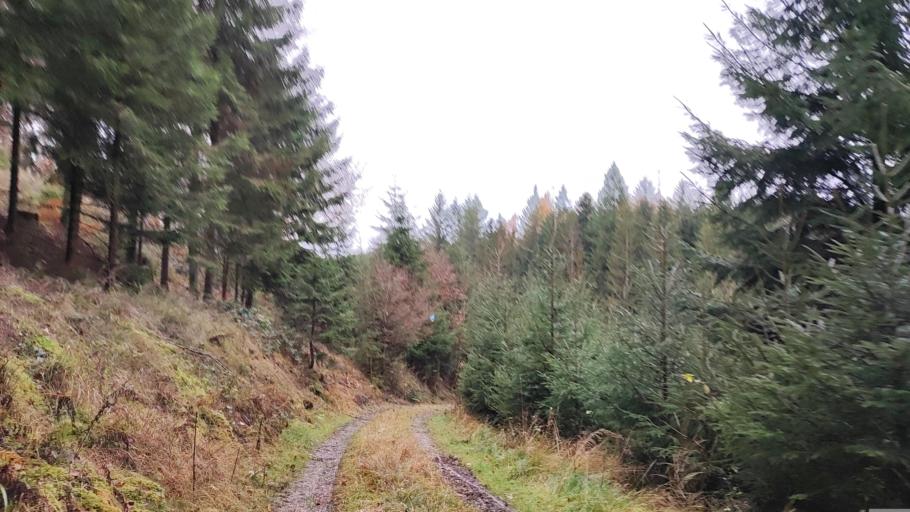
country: DE
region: Bavaria
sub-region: Swabia
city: Ziemetshausen
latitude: 48.3363
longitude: 10.5142
